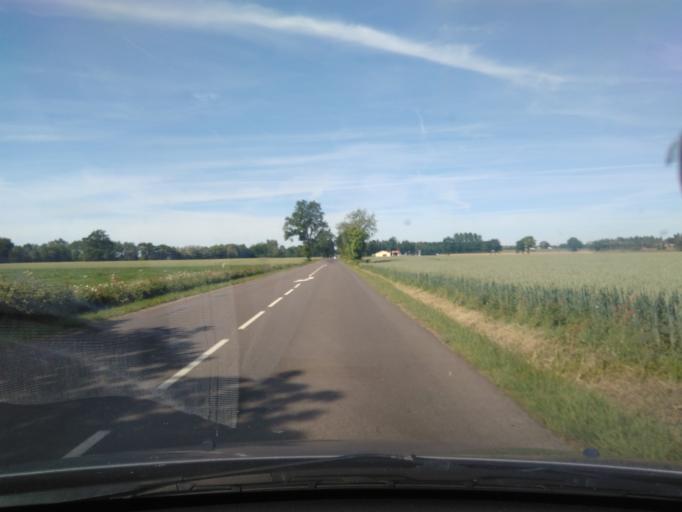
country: FR
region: Pays de la Loire
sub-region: Departement de la Vendee
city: Nieul-le-Dolent
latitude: 46.5270
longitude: -1.5499
